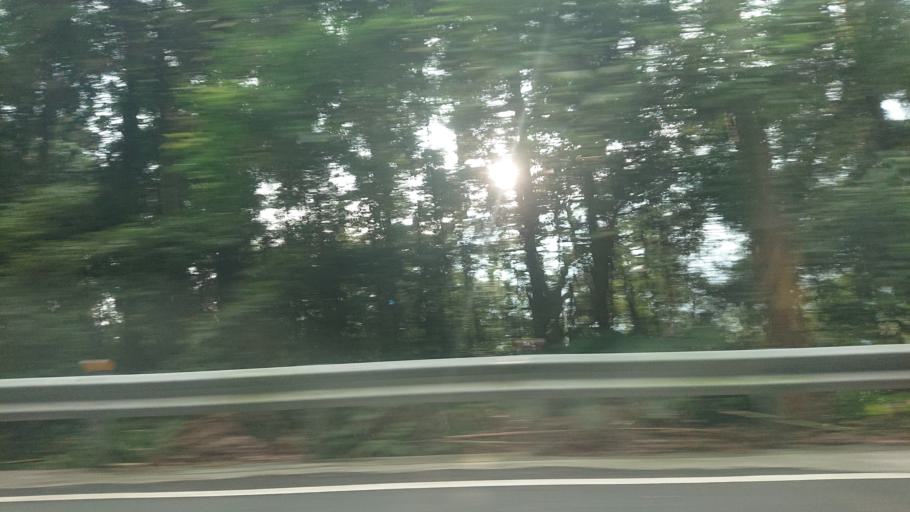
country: TW
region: Taiwan
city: Lugu
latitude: 23.4802
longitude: 120.7437
